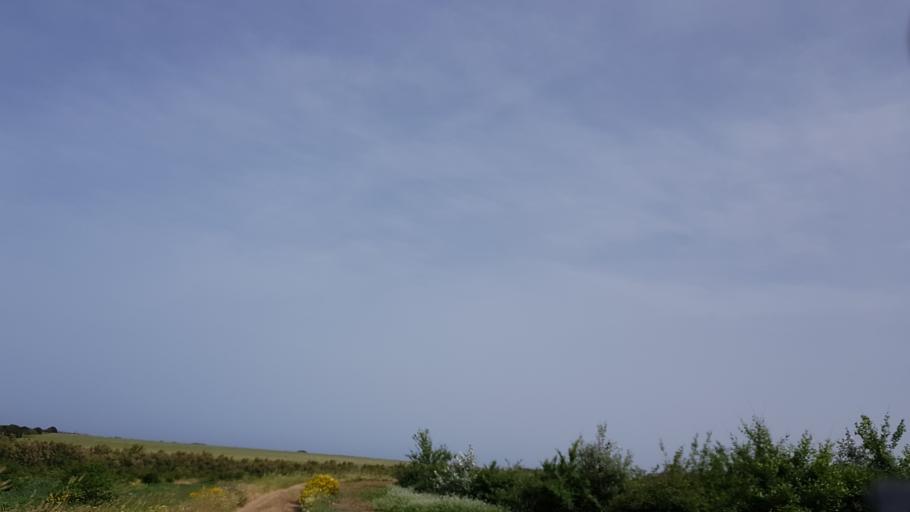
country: IT
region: Apulia
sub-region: Provincia di Brindisi
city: La Rosa
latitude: 40.5932
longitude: 18.0358
